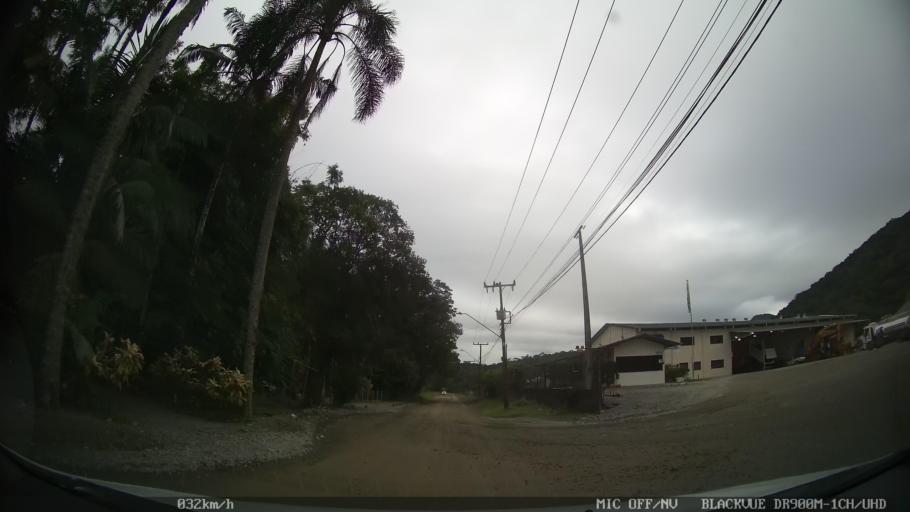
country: BR
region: Santa Catarina
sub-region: Joinville
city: Joinville
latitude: -26.2368
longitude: -48.9265
